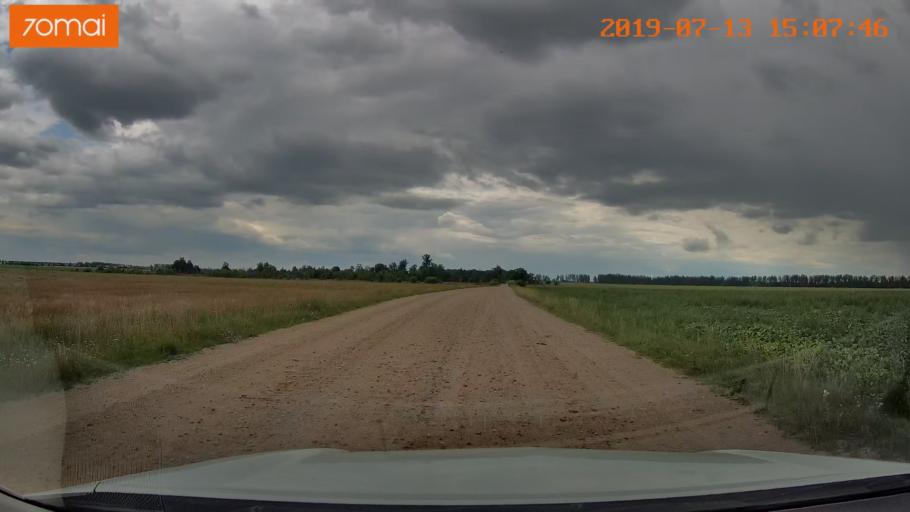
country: BY
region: Mogilev
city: Hlusha
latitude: 53.1867
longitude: 28.7570
